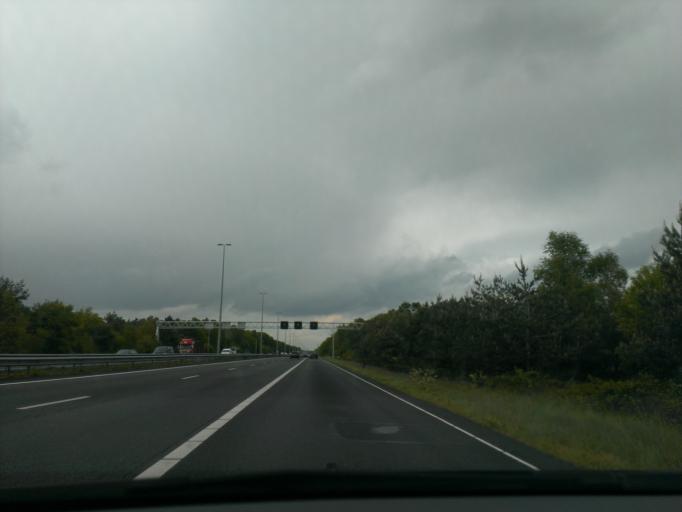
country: NL
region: Gelderland
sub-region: Gemeente Rozendaal
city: Rozendaal
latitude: 52.0732
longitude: 5.9453
